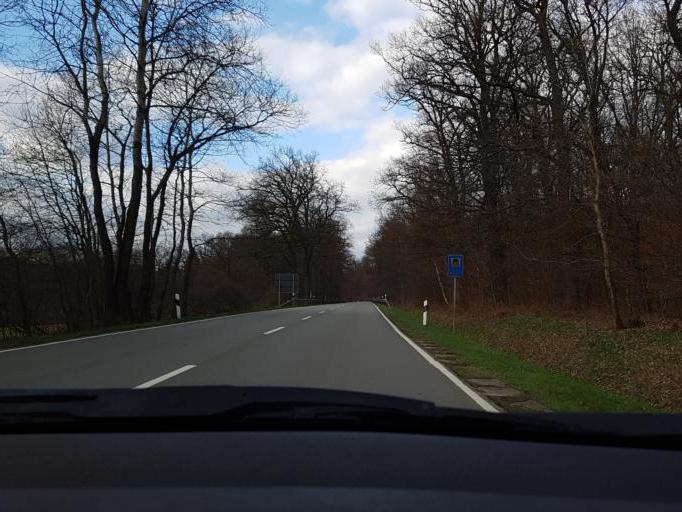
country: DE
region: Lower Saxony
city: Derental
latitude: 51.7291
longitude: 9.5118
